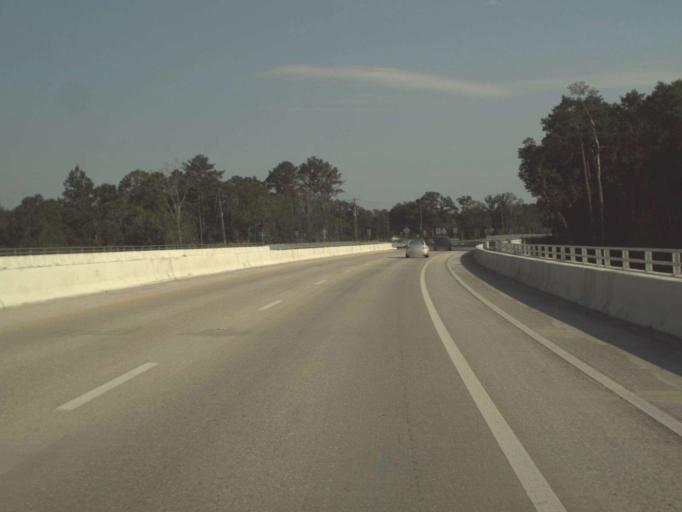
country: US
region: Florida
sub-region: Holmes County
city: Bonifay
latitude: 30.6280
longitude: -85.7121
